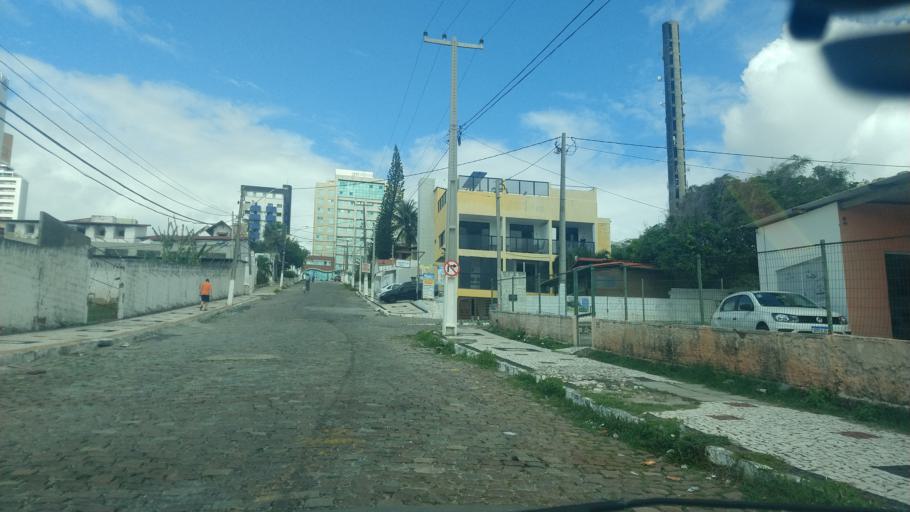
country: BR
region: Rio Grande do Norte
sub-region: Natal
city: Natal
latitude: -5.8716
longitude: -35.1787
